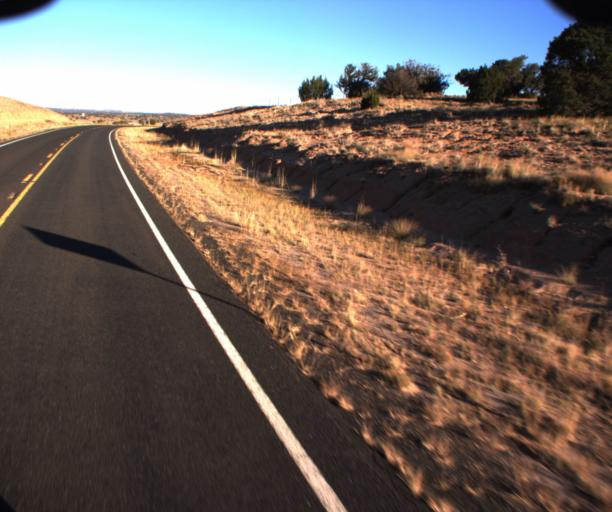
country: US
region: Arizona
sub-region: Apache County
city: Houck
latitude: 35.3809
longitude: -109.4942
